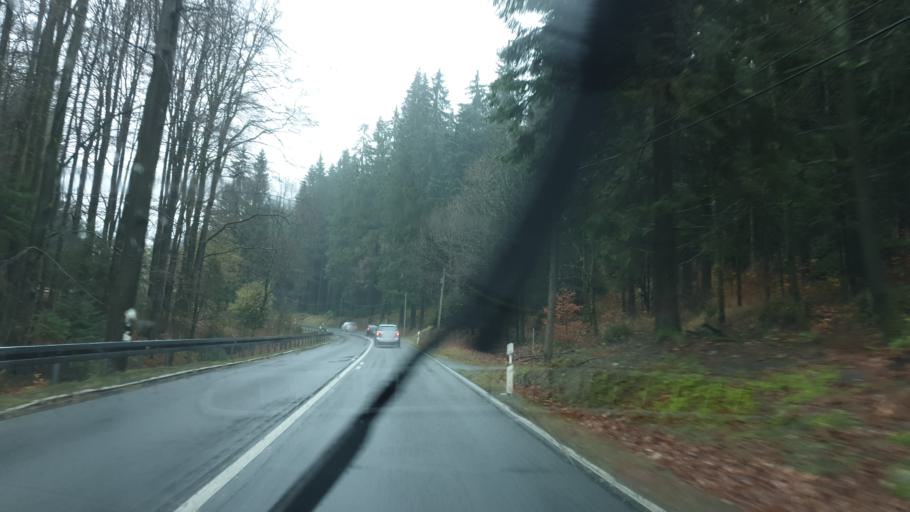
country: DE
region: Saxony
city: Tannenbergsthal
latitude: 50.4262
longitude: 12.4712
